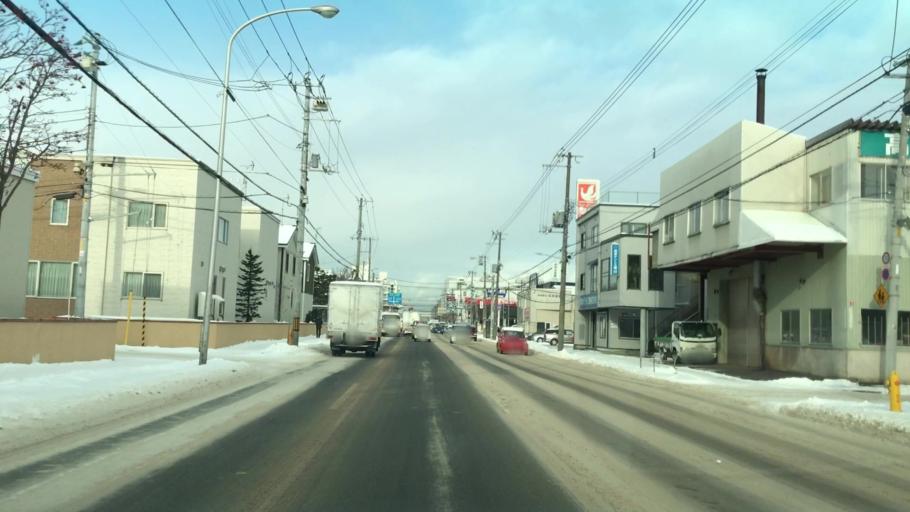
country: JP
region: Hokkaido
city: Sapporo
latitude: 43.0927
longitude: 141.3054
